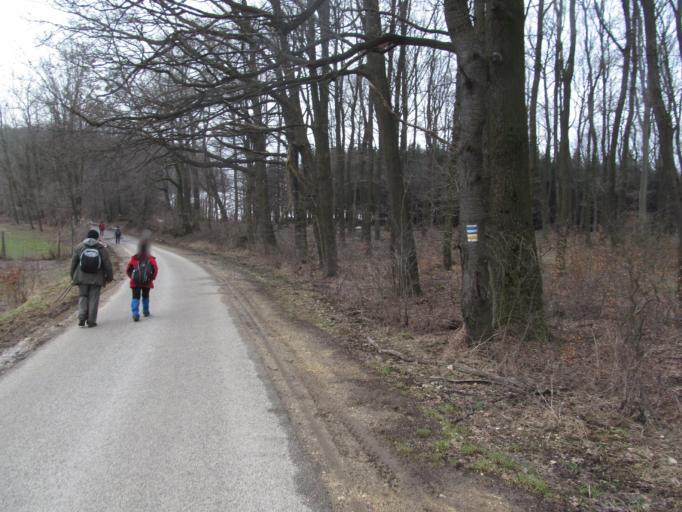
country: HU
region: Veszprem
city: Zirc
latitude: 47.2902
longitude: 17.8022
